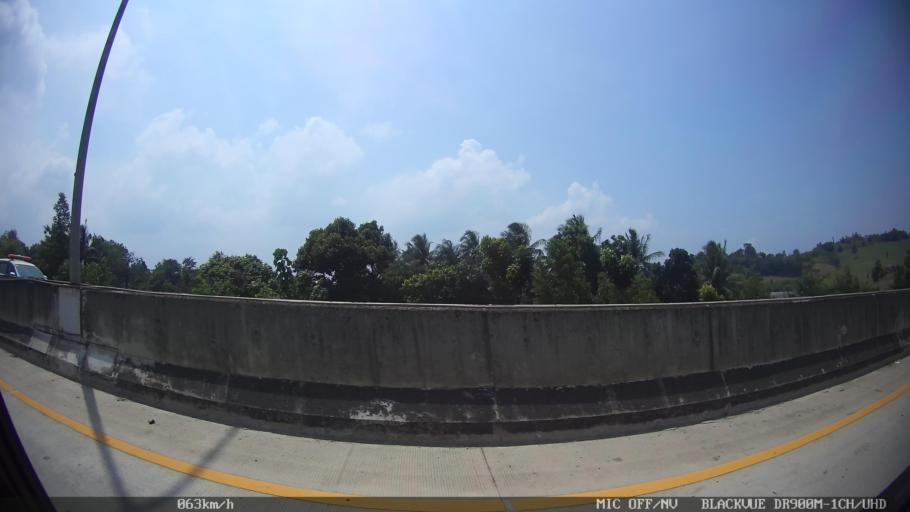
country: ID
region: Lampung
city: Panjang
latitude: -5.3986
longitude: 105.3471
